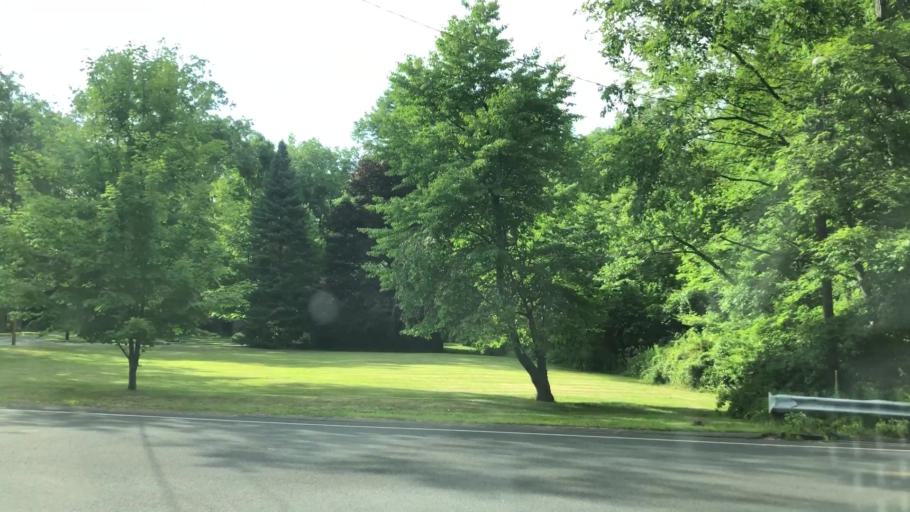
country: US
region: Massachusetts
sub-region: Hampshire County
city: Southampton
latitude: 42.2195
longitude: -72.7465
